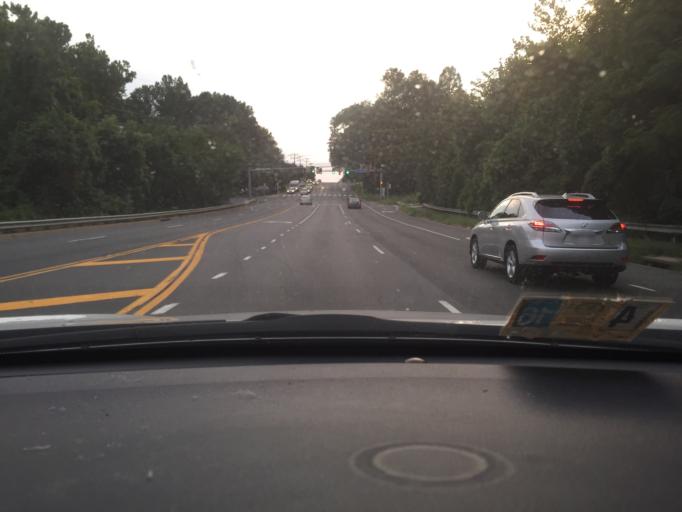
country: US
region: Virginia
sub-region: Fairfax County
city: Mantua
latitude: 38.8725
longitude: -77.2540
